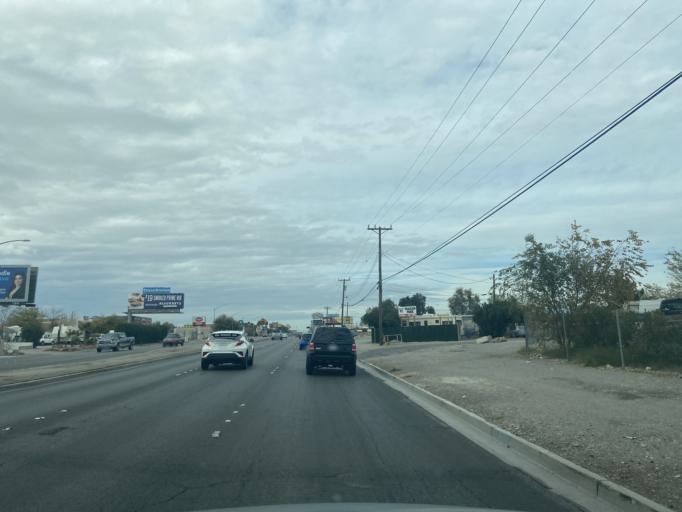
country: US
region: Nevada
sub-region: Clark County
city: Las Vegas
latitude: 36.1908
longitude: -115.1879
